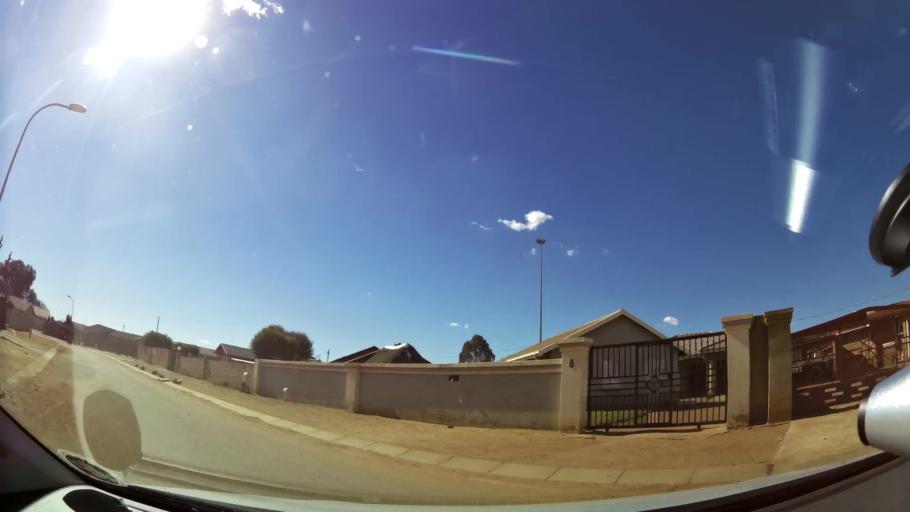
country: ZA
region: North-West
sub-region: Dr Kenneth Kaunda District Municipality
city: Klerksdorp
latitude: -26.8733
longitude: 26.5852
